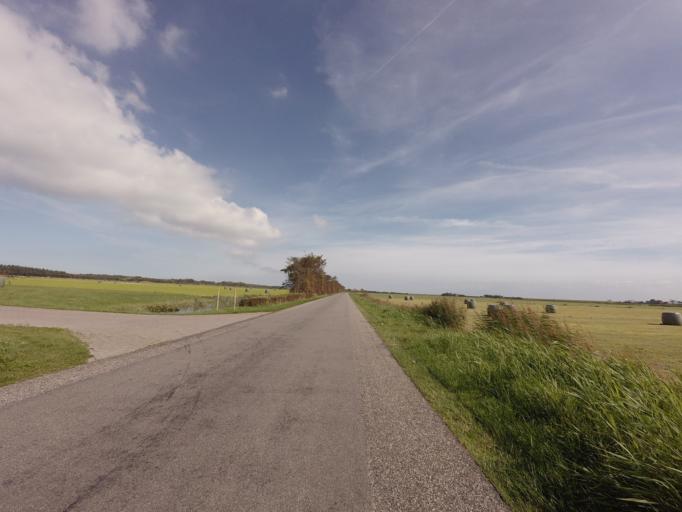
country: NL
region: Friesland
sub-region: Gemeente Ameland
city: Hollum
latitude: 53.4417
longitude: 5.6937
